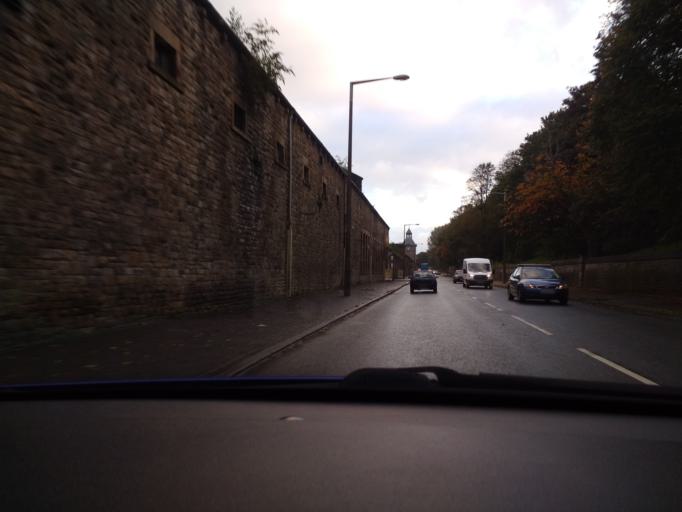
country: GB
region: England
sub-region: Lancashire
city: Lancaster
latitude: 54.0594
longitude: -2.7899
